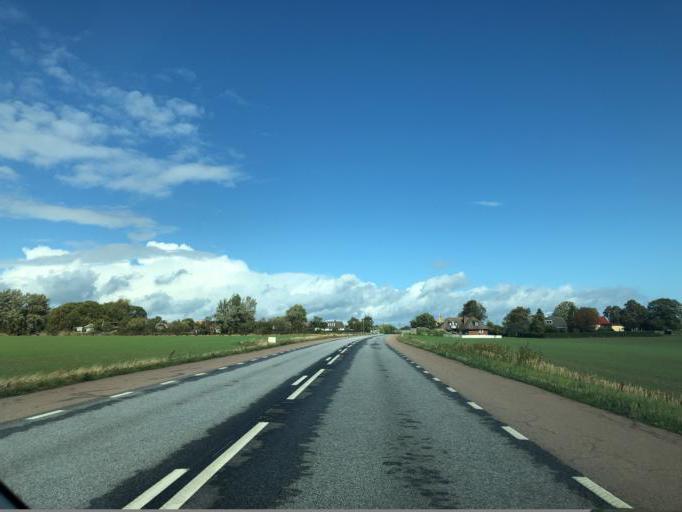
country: SE
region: Skane
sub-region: Helsingborg
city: Glumslov
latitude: 55.9150
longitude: 12.8294
